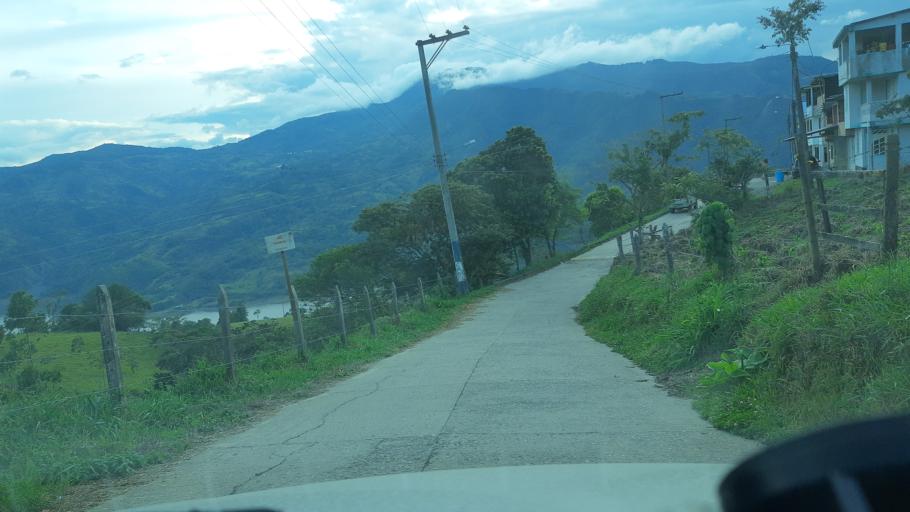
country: CO
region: Boyaca
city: Chivor
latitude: 4.9707
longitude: -73.3215
